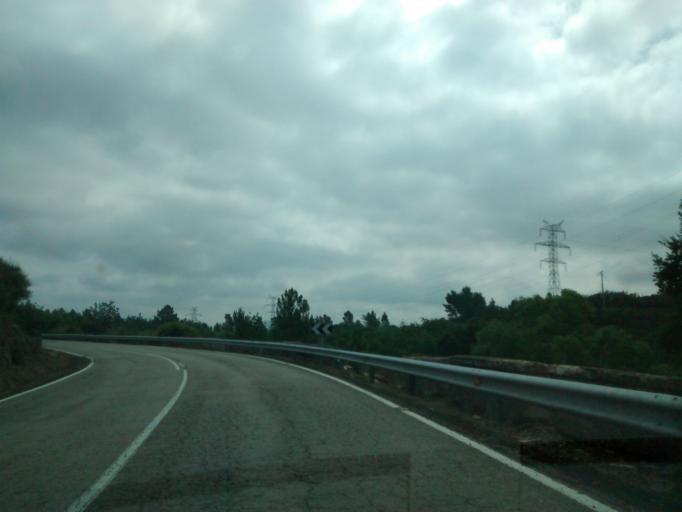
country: ES
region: Galicia
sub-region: Provincia de Ourense
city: Manzaneda
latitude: 42.3366
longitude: -7.1837
